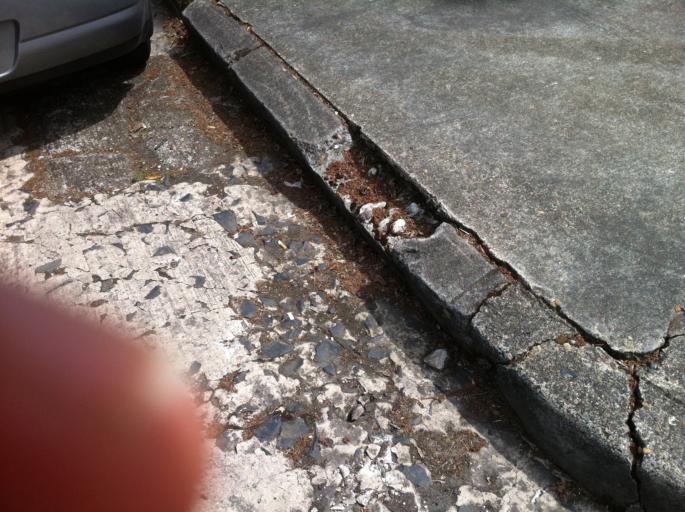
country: US
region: Oregon
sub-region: Multnomah County
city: Portland
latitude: 45.4825
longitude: -122.6757
